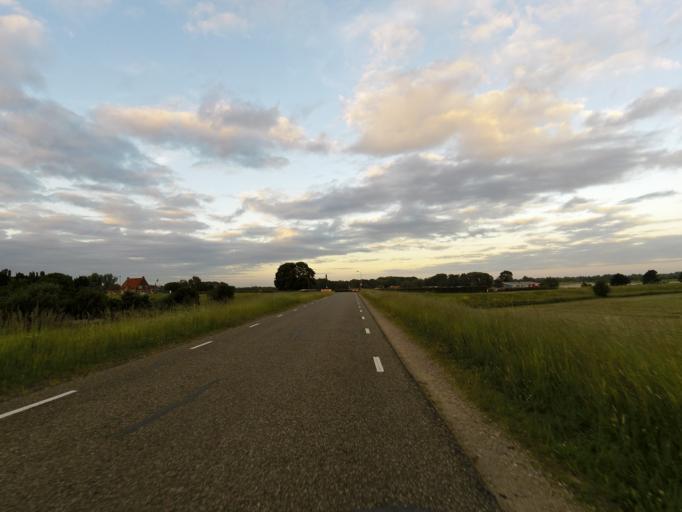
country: NL
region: Gelderland
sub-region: Gemeente Duiven
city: Duiven
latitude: 51.8757
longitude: 5.9856
